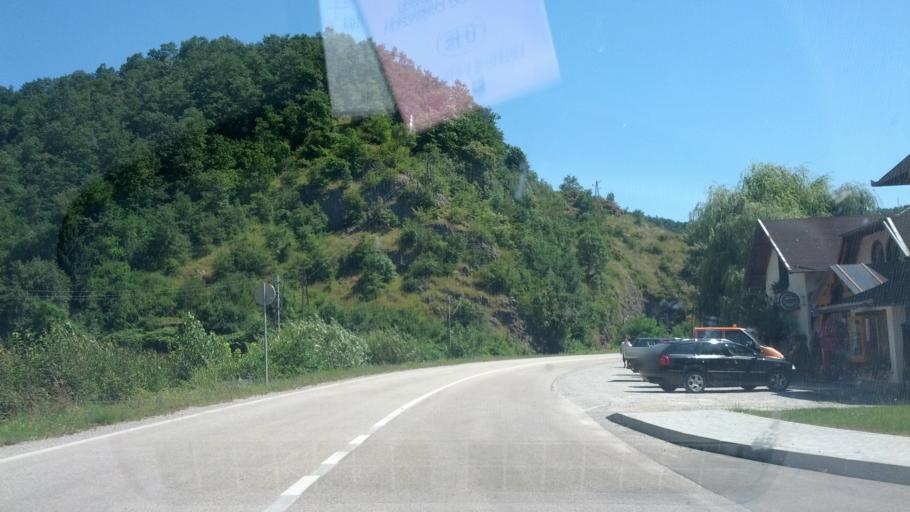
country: BA
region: Federation of Bosnia and Herzegovina
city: Bosanska Krupa
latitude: 44.8998
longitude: 16.1596
